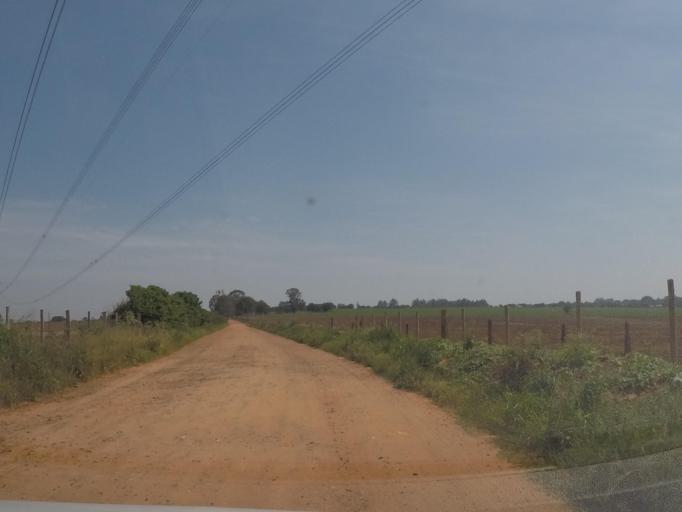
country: BR
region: Sao Paulo
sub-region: Sumare
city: Sumare
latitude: -22.8698
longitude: -47.2867
